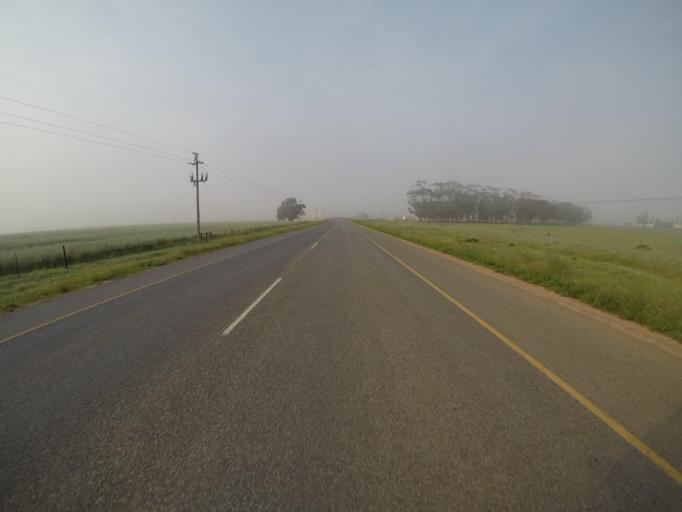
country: ZA
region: Western Cape
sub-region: City of Cape Town
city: Kraaifontein
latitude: -33.6640
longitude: 18.7078
